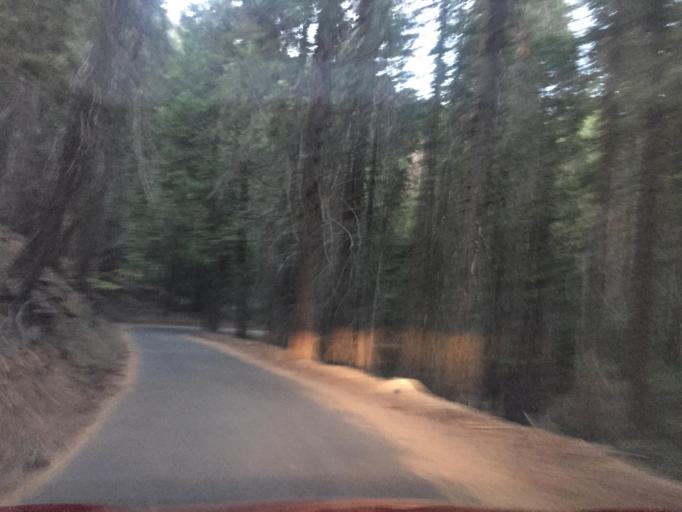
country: US
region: California
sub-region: Tulare County
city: Three Rivers
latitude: 36.4643
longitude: -118.6761
